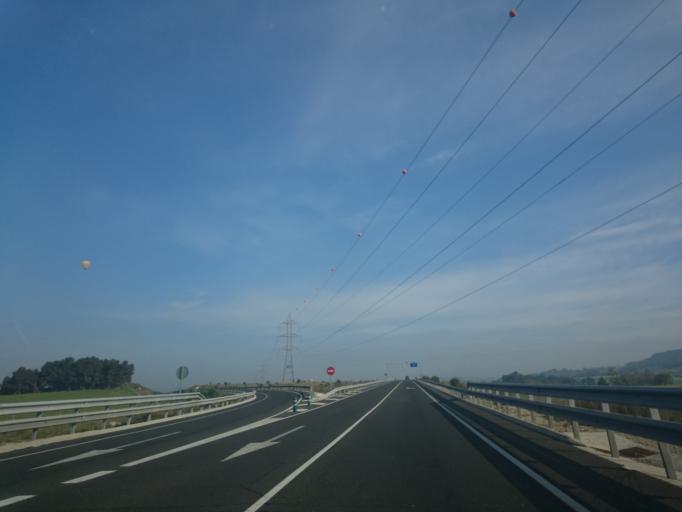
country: ES
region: Catalonia
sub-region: Provincia de Barcelona
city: Odena
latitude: 41.5865
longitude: 1.6643
